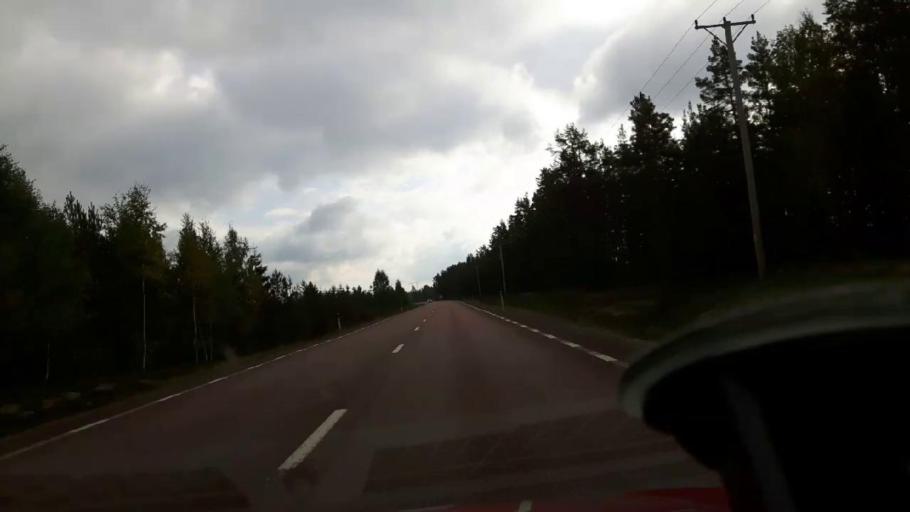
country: SE
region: Gaevleborg
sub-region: Soderhamns Kommun
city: Ljusne
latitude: 61.1021
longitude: 16.9465
